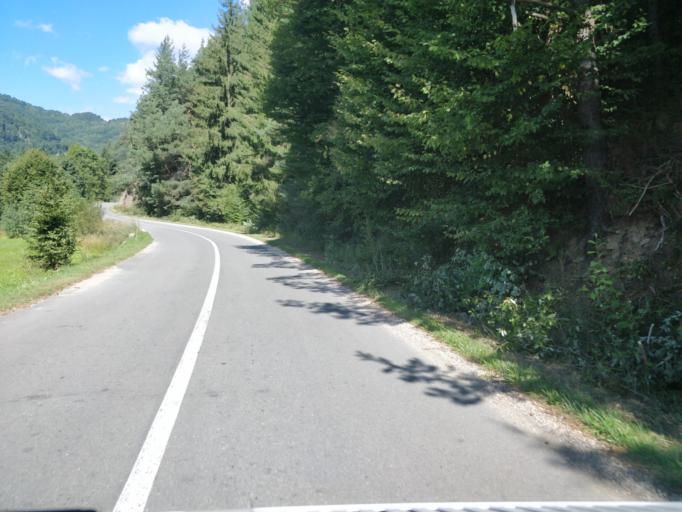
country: RO
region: Cluj
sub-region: Comuna Sacueu
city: Sacuieu
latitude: 46.8303
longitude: 22.8749
